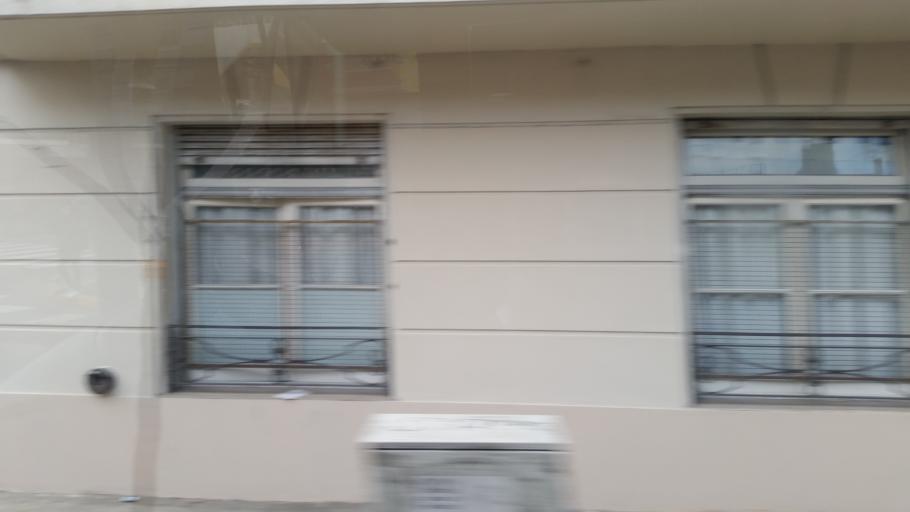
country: AR
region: Buenos Aires F.D.
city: Colegiales
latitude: -34.6070
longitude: -58.4303
